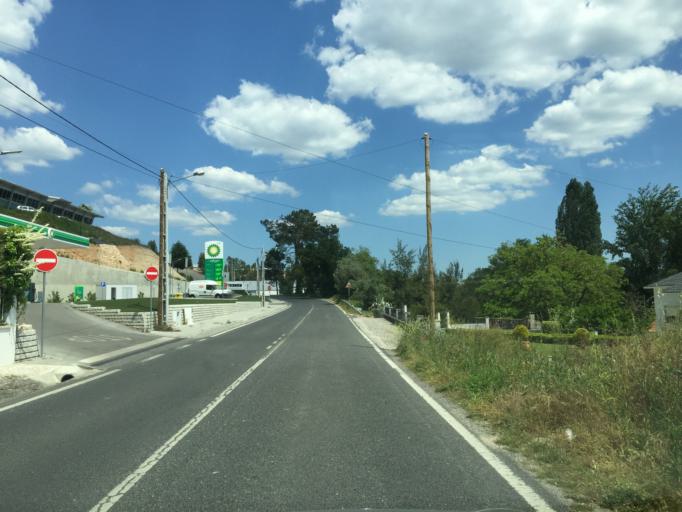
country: PT
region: Santarem
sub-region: Ourem
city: Ourem
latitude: 39.6544
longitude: -8.5978
